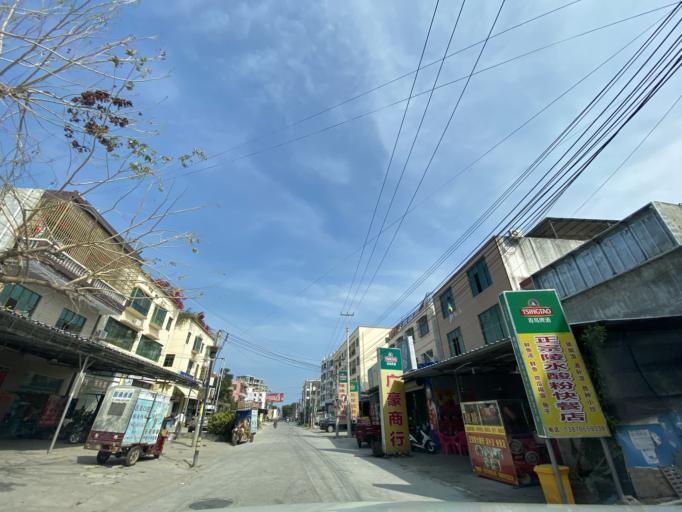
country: CN
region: Hainan
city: Yingzhou
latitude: 18.4038
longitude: 109.8424
